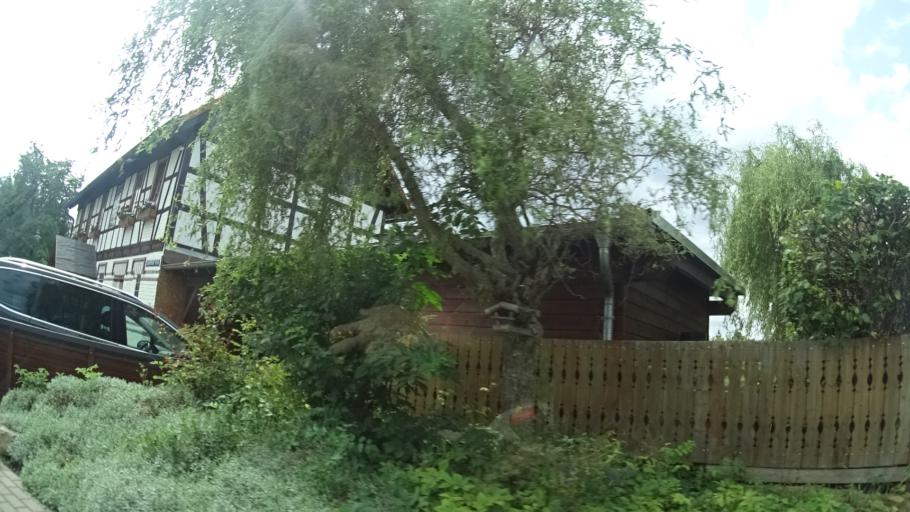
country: DE
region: Thuringia
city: Unterwellenborn
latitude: 50.6603
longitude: 11.4233
